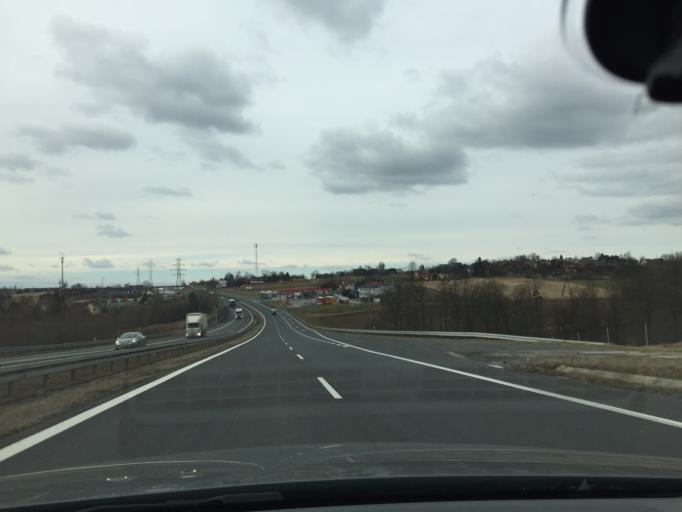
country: PL
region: Silesian Voivodeship
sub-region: Powiat cieszynski
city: Zamarski
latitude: 49.7654
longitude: 18.6583
